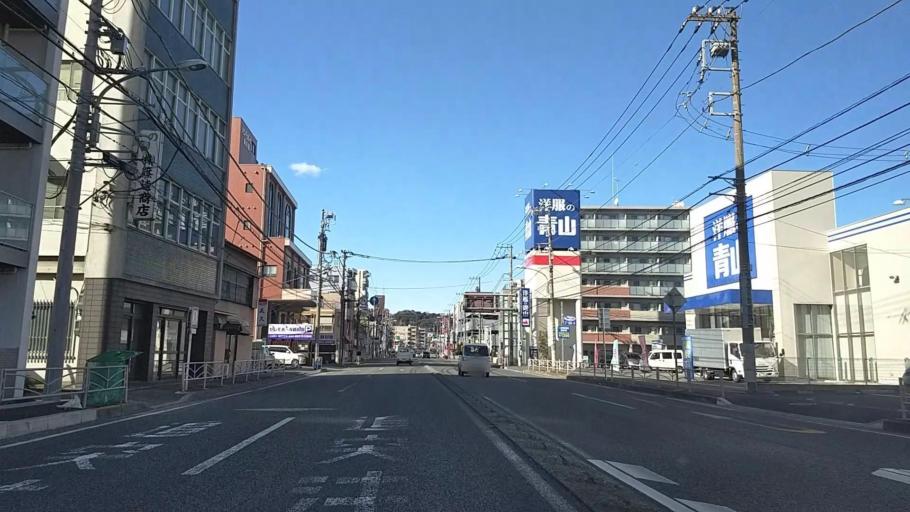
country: JP
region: Kanagawa
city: Yokohama
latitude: 35.3877
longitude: 139.6172
